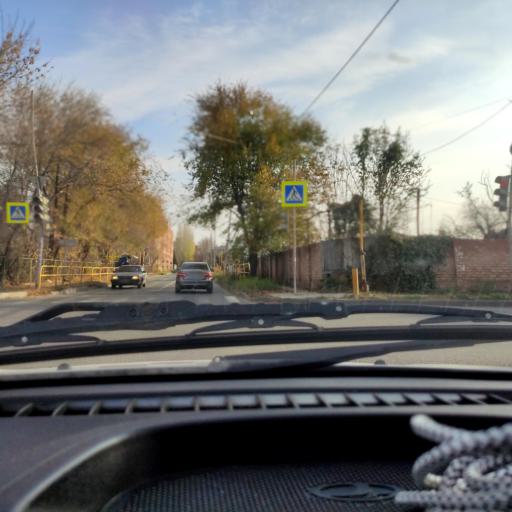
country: RU
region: Samara
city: Tol'yatti
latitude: 53.5131
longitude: 49.4014
